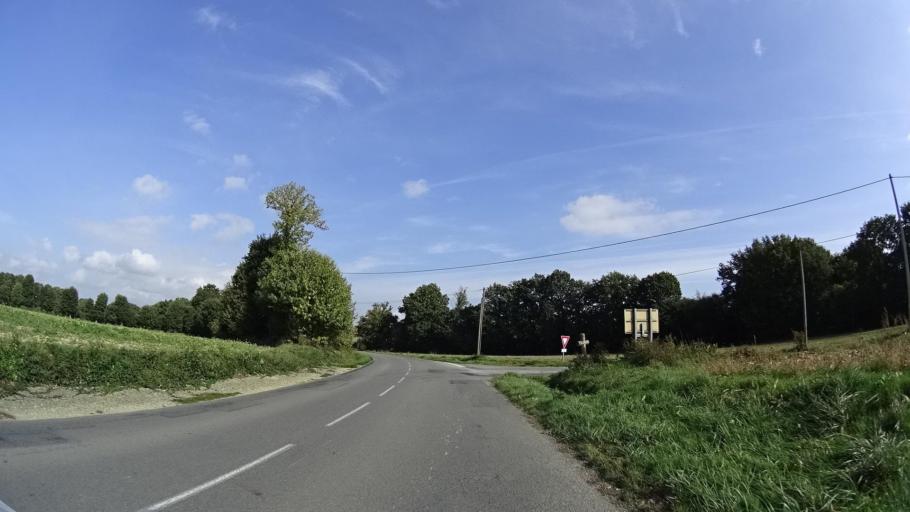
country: FR
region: Brittany
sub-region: Departement d'Ille-et-Vilaine
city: Quedillac
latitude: 48.2354
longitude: -2.1609
